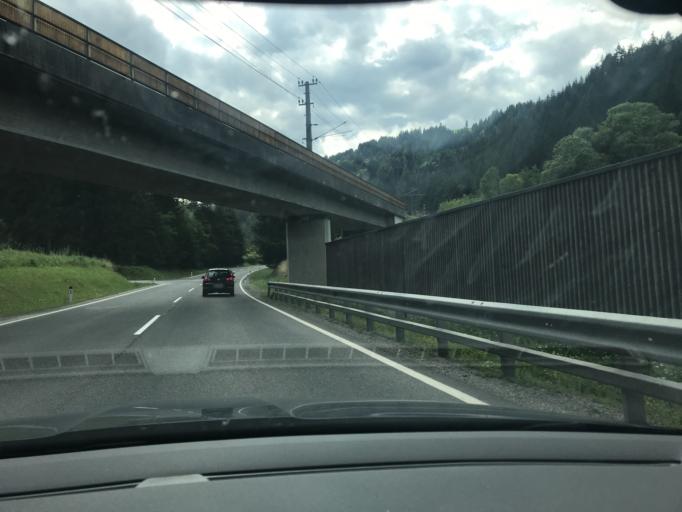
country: AT
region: Tyrol
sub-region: Politischer Bezirk Lienz
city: Anras
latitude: 46.7688
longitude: 12.5864
